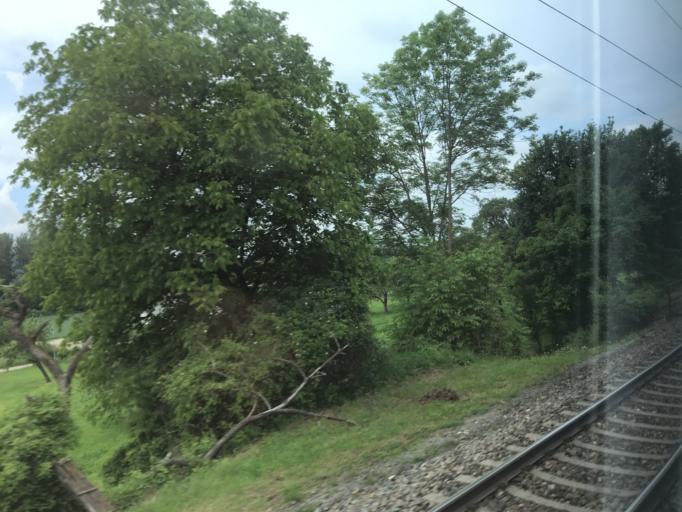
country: DE
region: Baden-Wuerttemberg
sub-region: Regierungsbezirk Stuttgart
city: Gingen an der Fils
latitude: 48.6702
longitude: 9.7790
